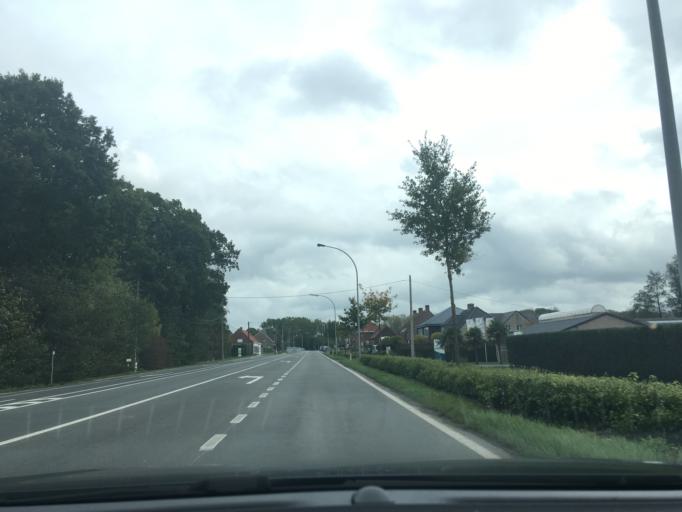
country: BE
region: Flanders
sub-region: Provincie West-Vlaanderen
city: Zonnebeke
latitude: 50.8455
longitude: 2.9514
